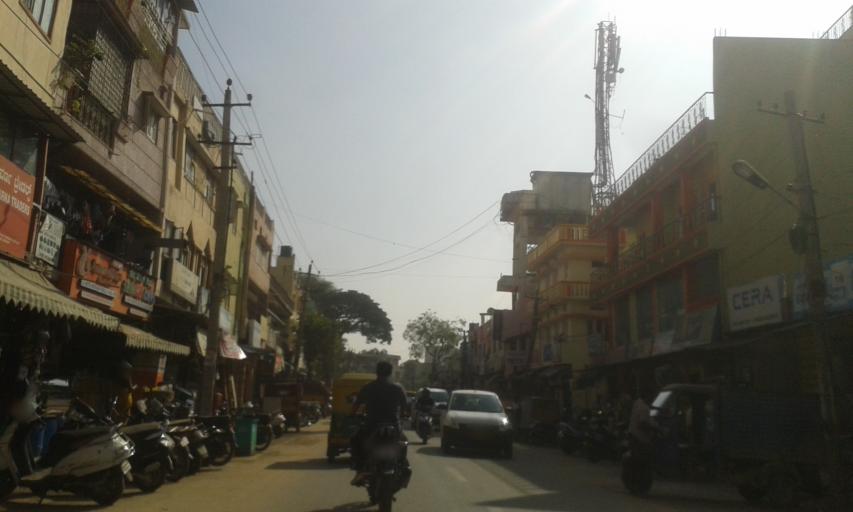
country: IN
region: Karnataka
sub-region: Bangalore Urban
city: Bangalore
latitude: 12.9505
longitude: 77.6246
